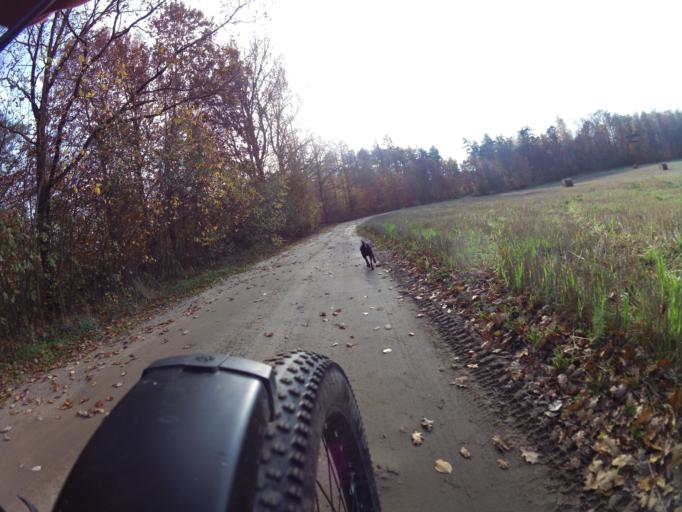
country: PL
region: Pomeranian Voivodeship
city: Strzelno
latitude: 54.7433
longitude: 18.2849
